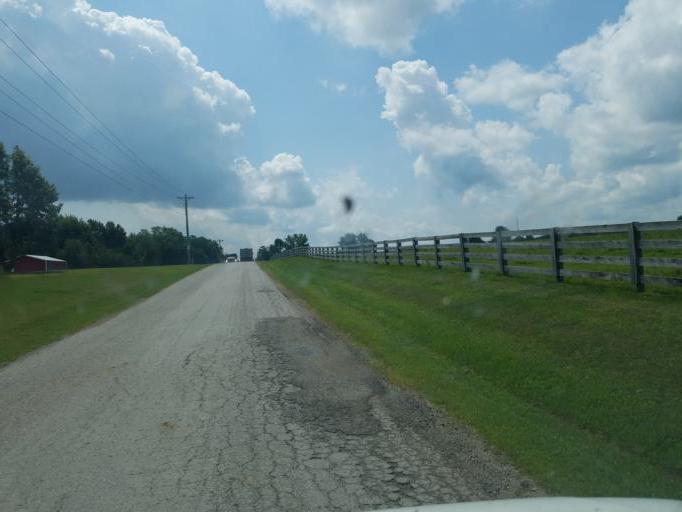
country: US
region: Ohio
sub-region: Knox County
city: Centerburg
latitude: 40.3961
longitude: -82.6525
